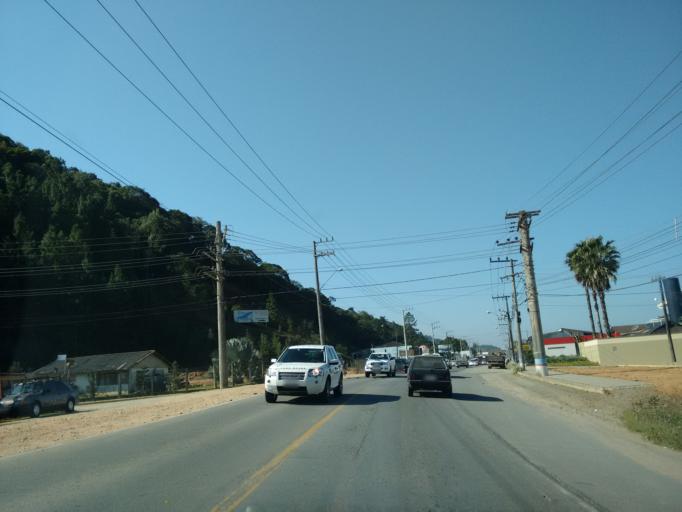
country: BR
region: Santa Catarina
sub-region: Guaramirim
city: Guaramirim
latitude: -26.4749
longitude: -49.0302
